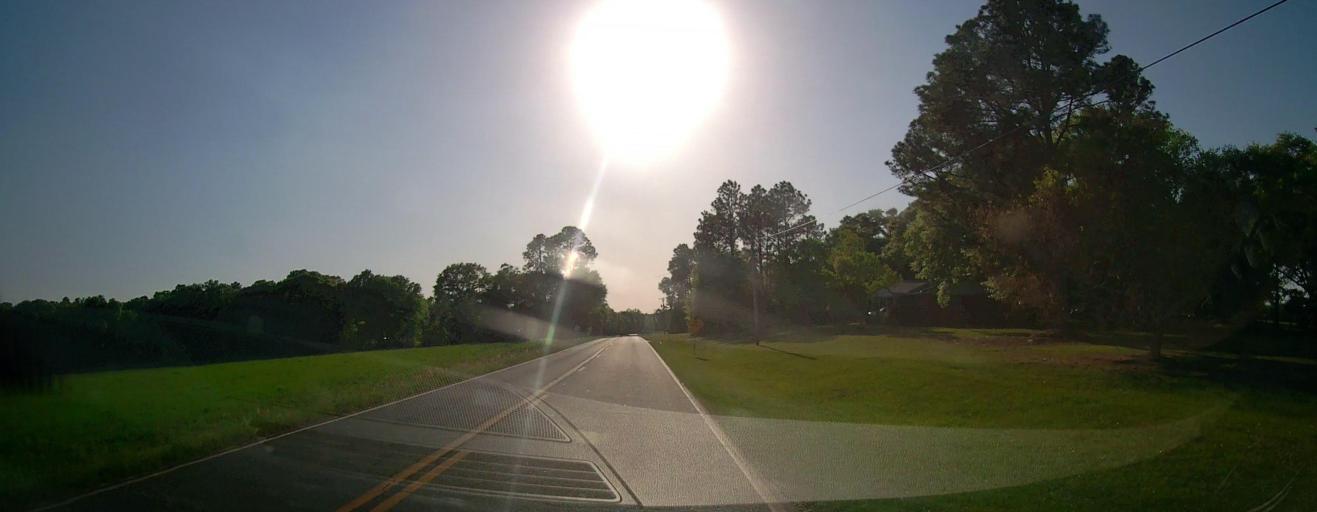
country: US
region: Georgia
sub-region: Macon County
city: Montezuma
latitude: 32.3143
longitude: -83.9967
